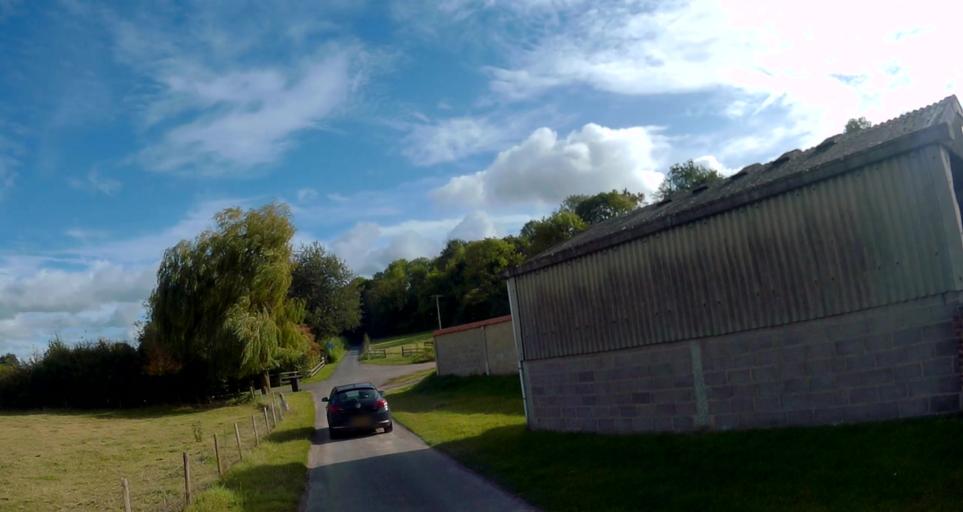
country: GB
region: England
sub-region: Hampshire
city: Kings Worthy
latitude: 51.0865
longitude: -1.2170
